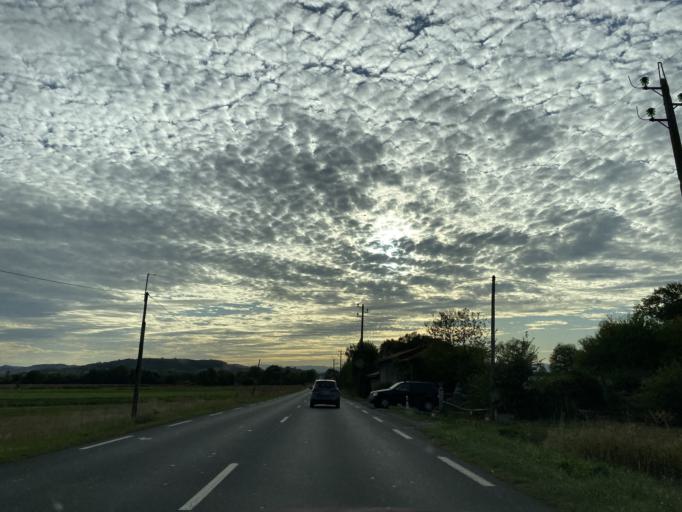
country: FR
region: Auvergne
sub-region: Departement du Puy-de-Dome
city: Lezoux
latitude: 45.8225
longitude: 3.3593
